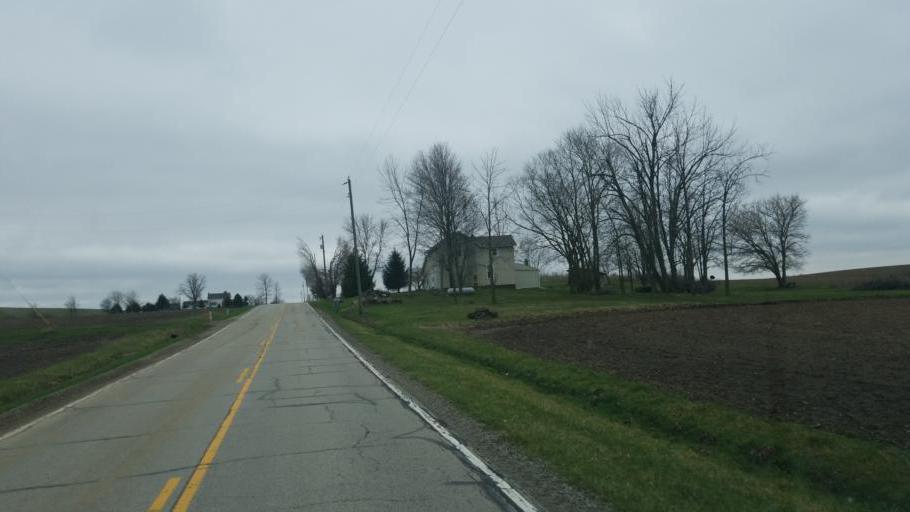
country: US
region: Ohio
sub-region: Crawford County
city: Bucyrus
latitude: 40.8466
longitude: -82.9403
